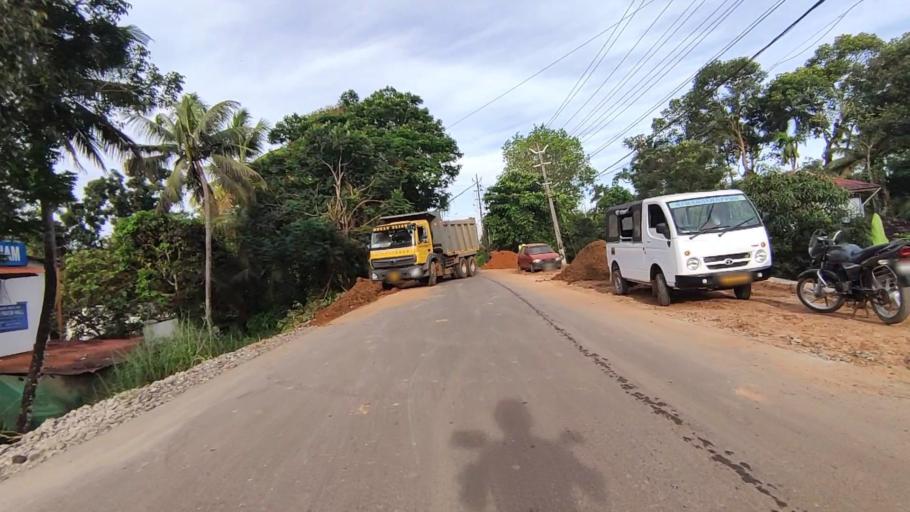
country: IN
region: Kerala
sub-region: Kottayam
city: Kottayam
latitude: 9.6103
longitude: 76.4929
